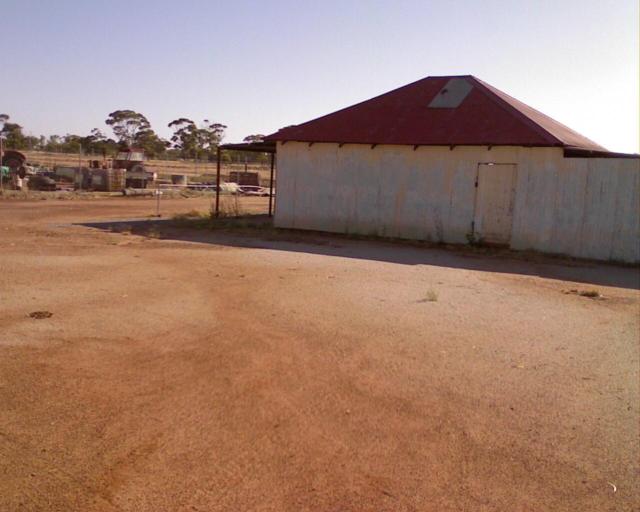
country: AU
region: Western Australia
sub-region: Merredin
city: Merredin
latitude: -31.1120
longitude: 117.7893
